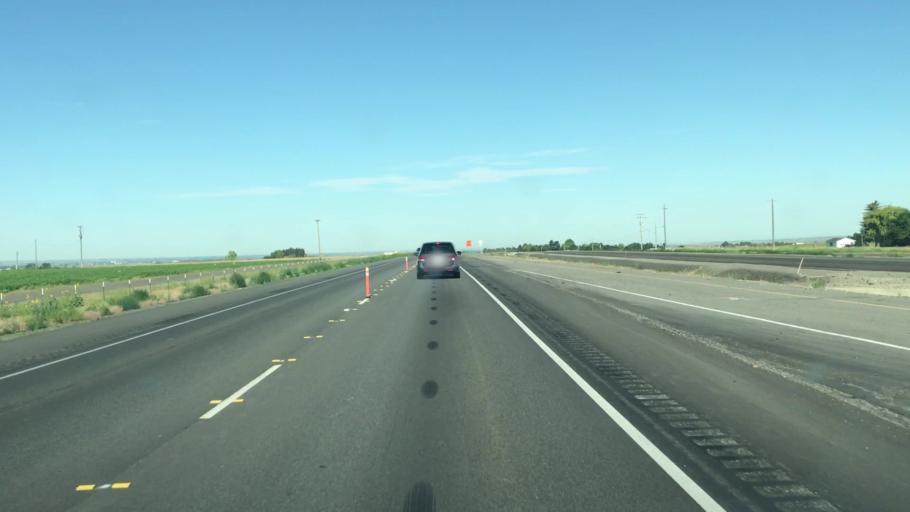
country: US
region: Idaho
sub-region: Twin Falls County
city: Hansen
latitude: 42.5762
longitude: -114.2665
